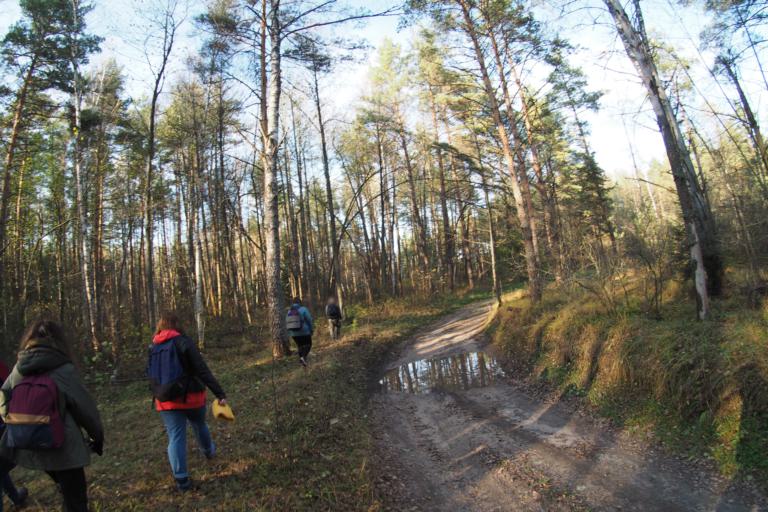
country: RU
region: Moskovskaya
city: Davydovo
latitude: 55.5444
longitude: 38.8275
